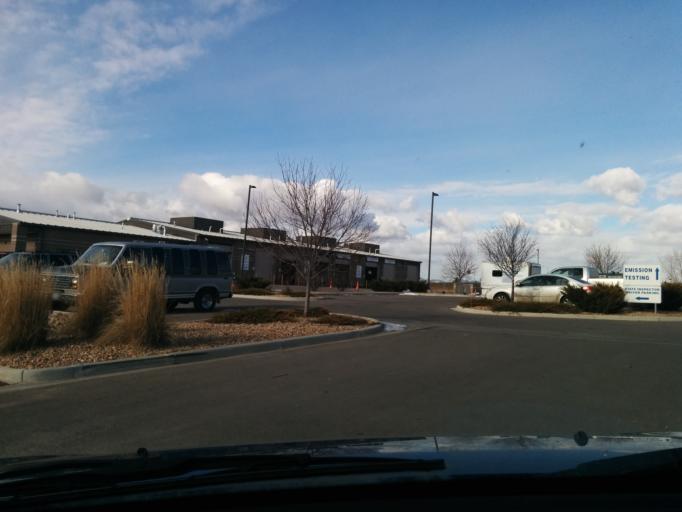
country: US
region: Colorado
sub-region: Larimer County
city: Fort Collins
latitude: 40.5791
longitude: -104.9985
